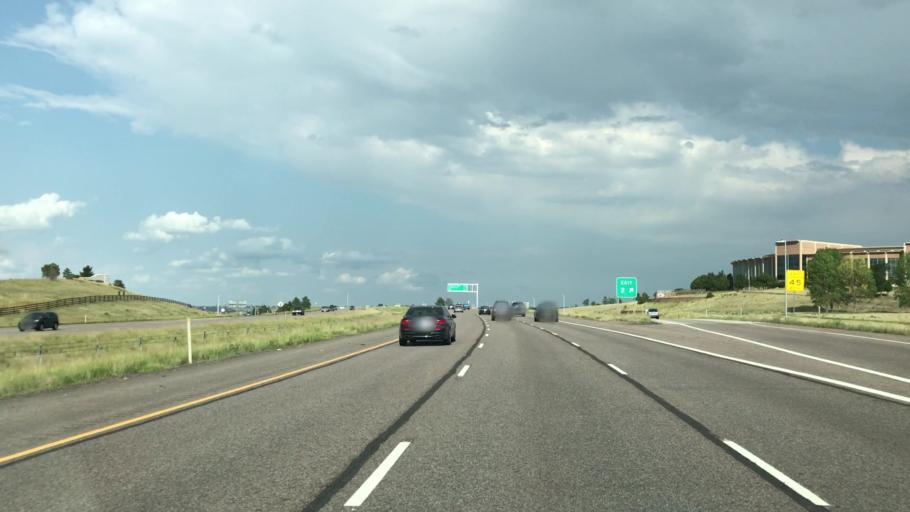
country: US
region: Colorado
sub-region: Douglas County
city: Meridian
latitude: 39.5505
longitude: -104.8474
